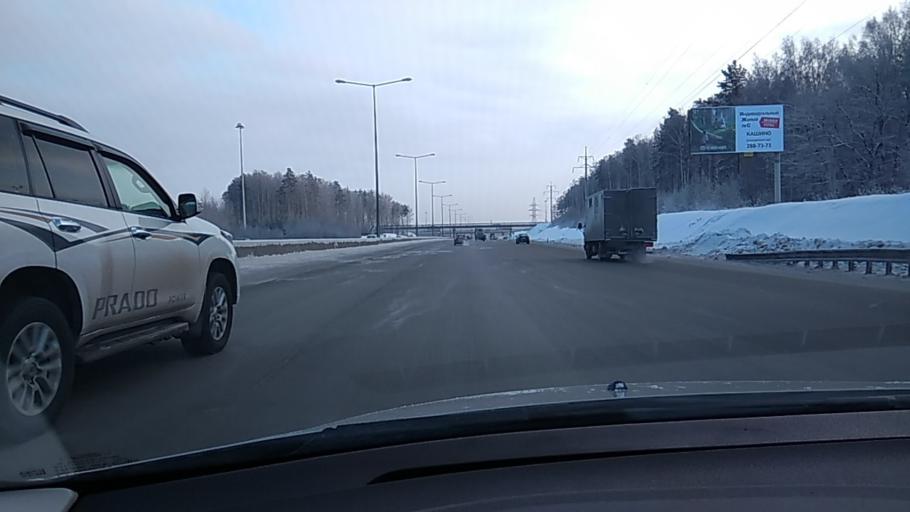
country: RU
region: Sverdlovsk
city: Istok
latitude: 56.7712
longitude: 60.7271
